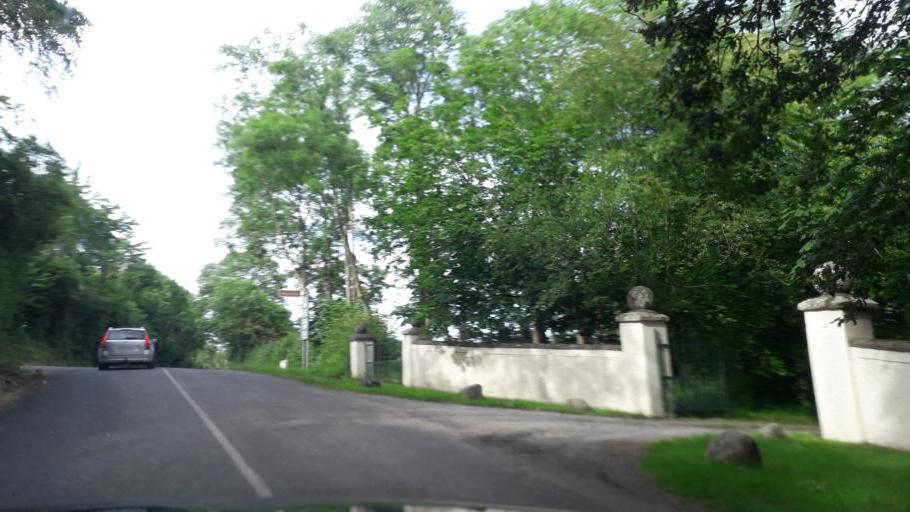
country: IE
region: Leinster
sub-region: Loch Garman
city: Courtown
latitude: 52.5470
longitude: -6.2528
